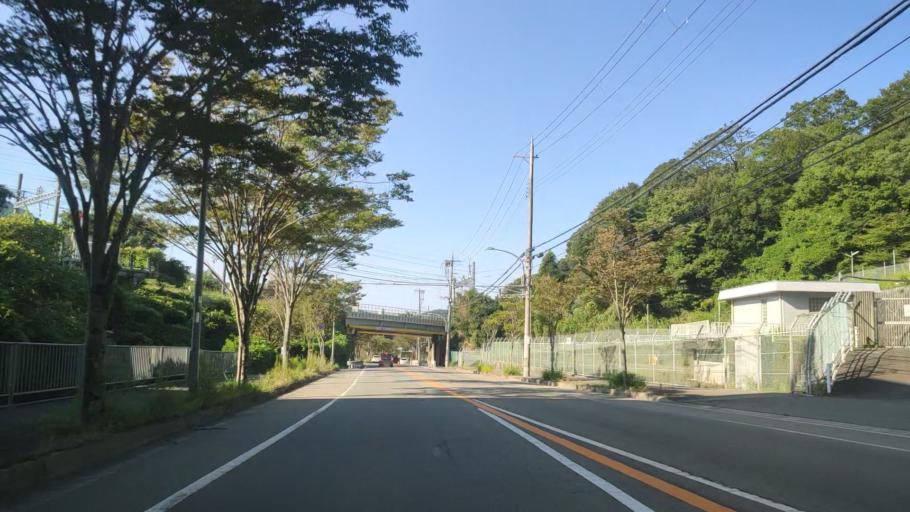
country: JP
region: Hyogo
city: Kobe
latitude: 34.7726
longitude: 135.1922
